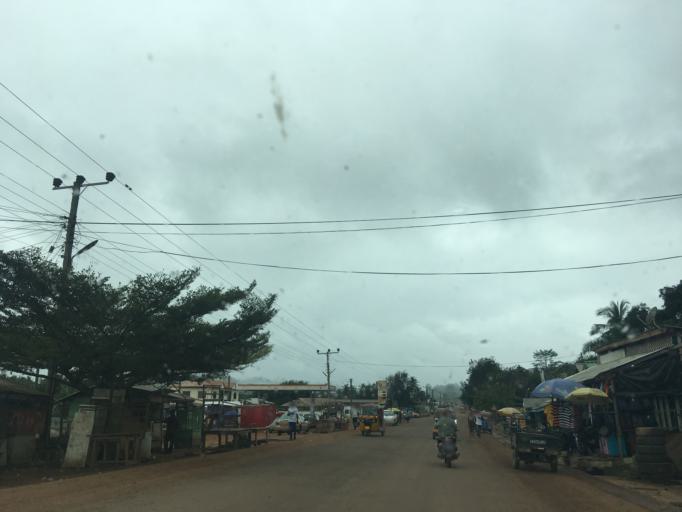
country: GH
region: Western
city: Wassa-Akropong
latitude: 5.8057
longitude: -2.4328
